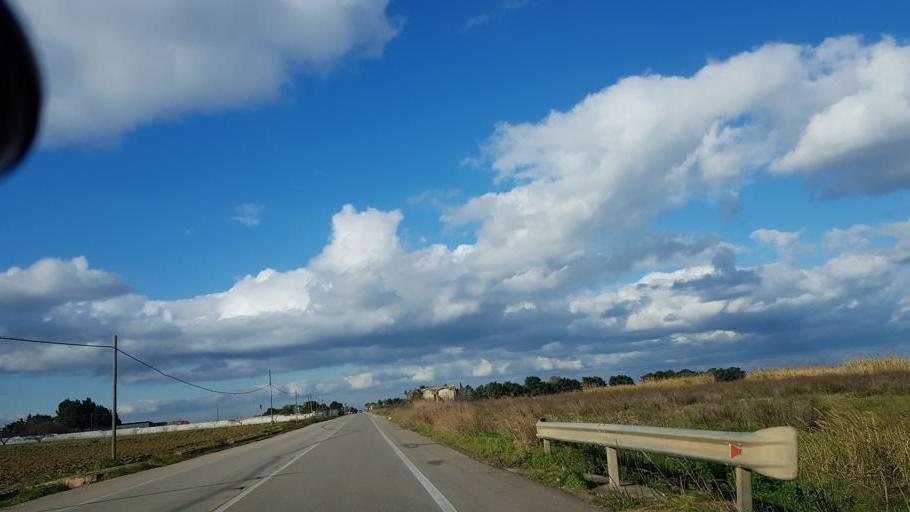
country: IT
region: Apulia
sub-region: Provincia di Brindisi
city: Brindisi
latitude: 40.6467
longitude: 17.8888
